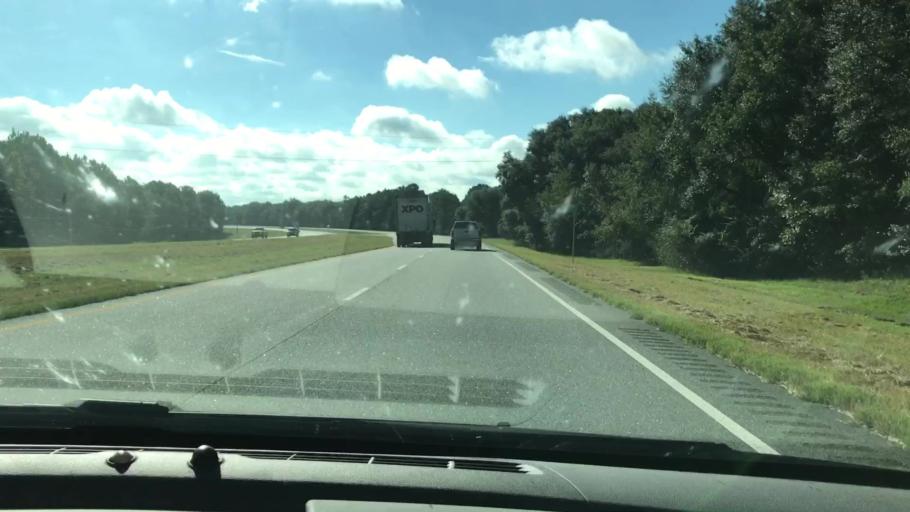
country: US
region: Georgia
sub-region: Dougherty County
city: Putney
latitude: 31.5581
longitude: -84.0067
